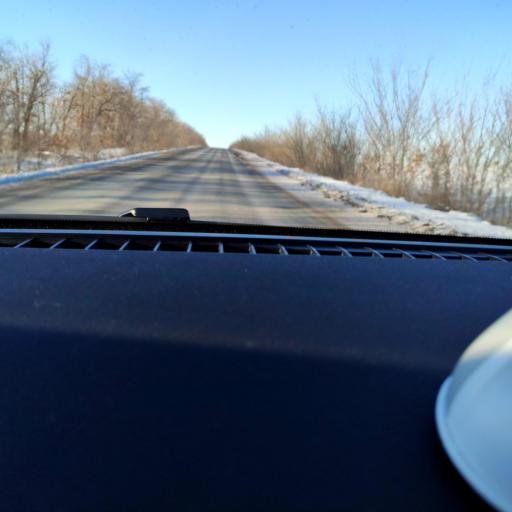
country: RU
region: Samara
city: Spiridonovka
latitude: 53.1446
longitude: 50.5364
